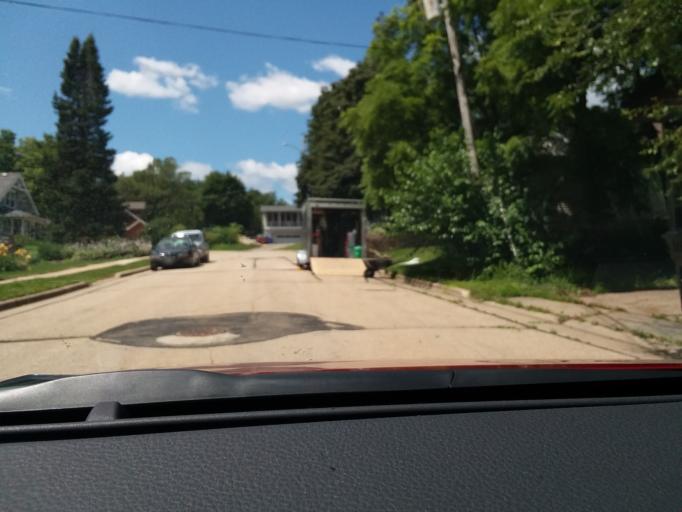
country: US
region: Wisconsin
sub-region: Dane County
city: De Forest
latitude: 43.2443
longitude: -89.3423
